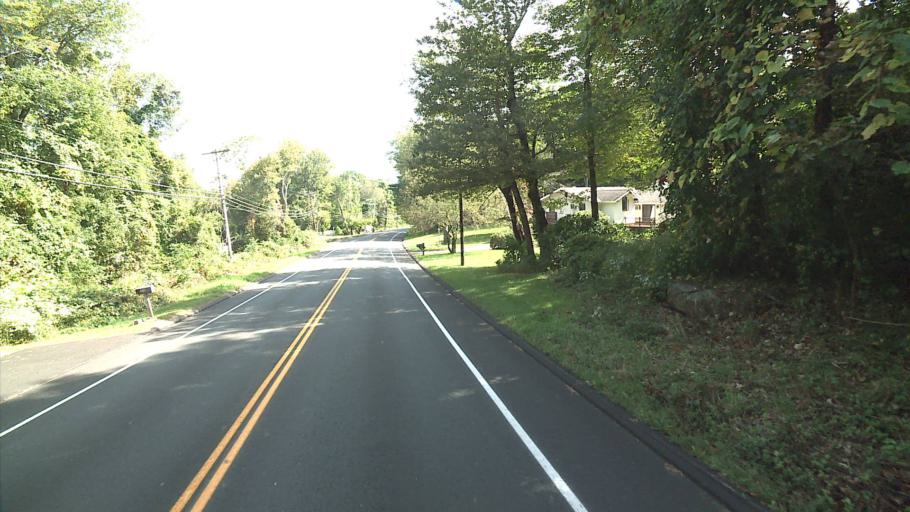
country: US
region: Connecticut
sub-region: Fairfield County
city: Newtown
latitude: 41.3909
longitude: -73.2178
